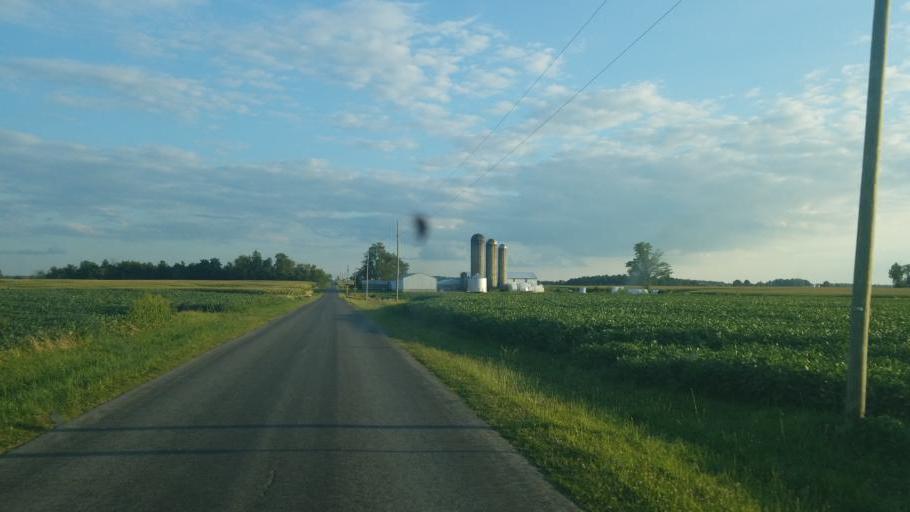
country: US
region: Ohio
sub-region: Huron County
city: Greenwich
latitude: 41.0087
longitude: -82.5591
